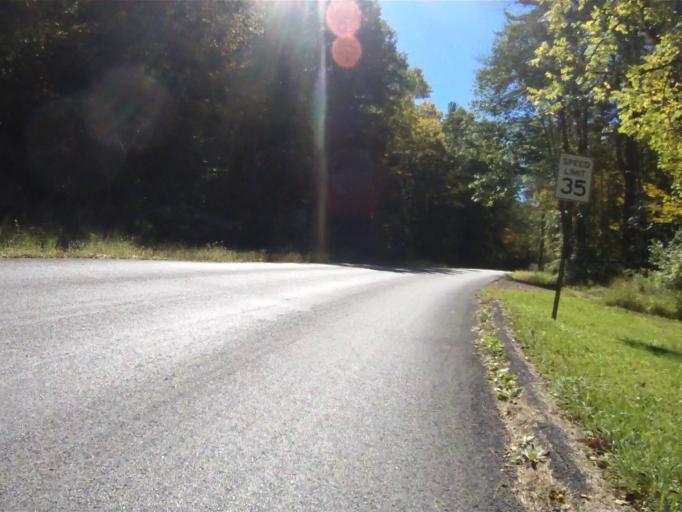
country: US
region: Pennsylvania
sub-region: Centre County
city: Houserville
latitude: 40.9032
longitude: -77.8719
